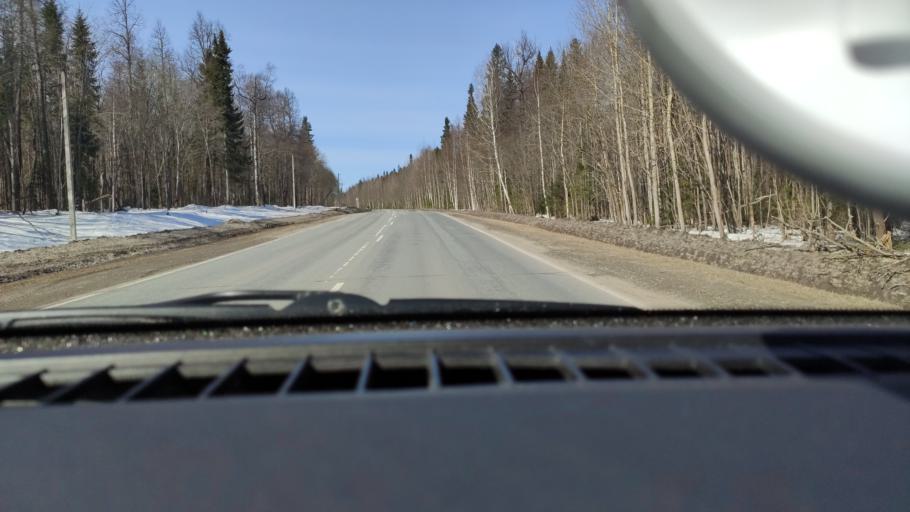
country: RU
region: Perm
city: Perm
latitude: 58.2058
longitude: 56.1980
